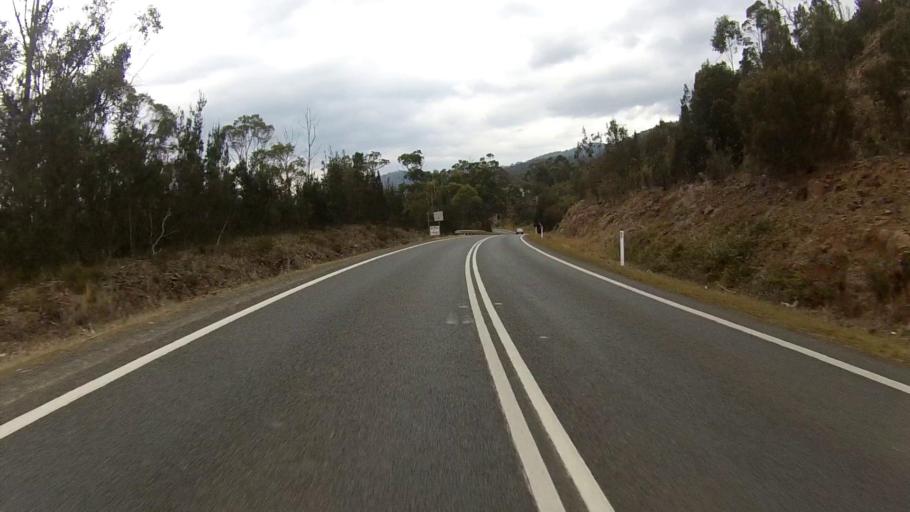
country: AU
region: Tasmania
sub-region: Huon Valley
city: Huonville
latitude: -43.0418
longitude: 147.0535
